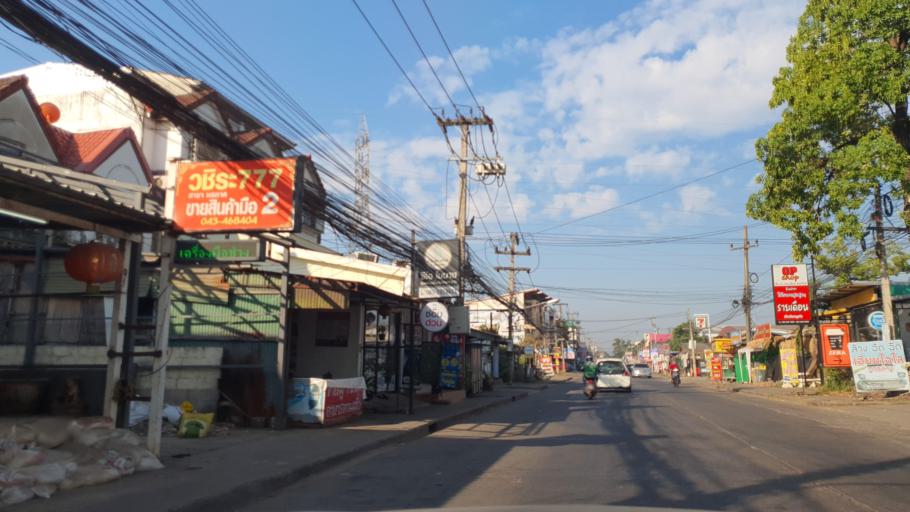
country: TH
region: Khon Kaen
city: Khon Kaen
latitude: 16.4214
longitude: 102.8145
